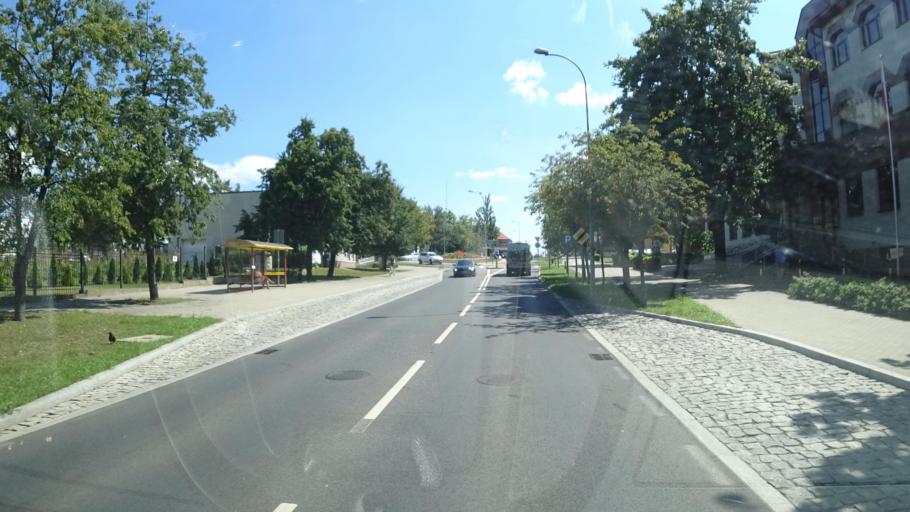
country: PL
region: Podlasie
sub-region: Lomza
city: Lomza
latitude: 53.1757
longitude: 22.0777
